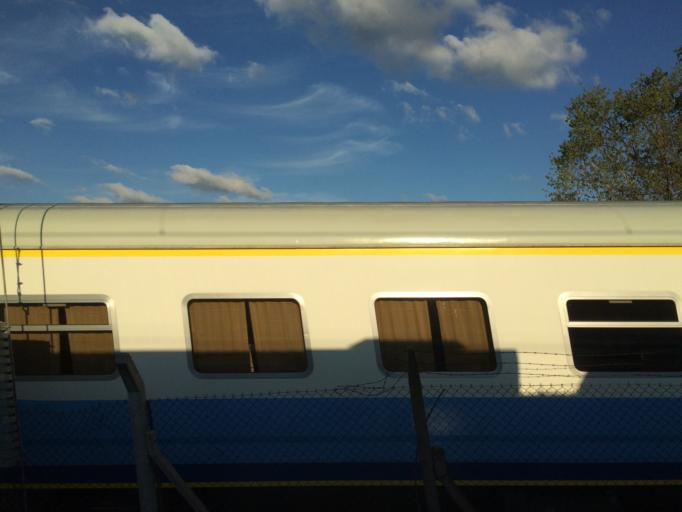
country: AR
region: Buenos Aires
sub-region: Partido de Lanus
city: Lanus
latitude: -34.7298
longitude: -58.3938
